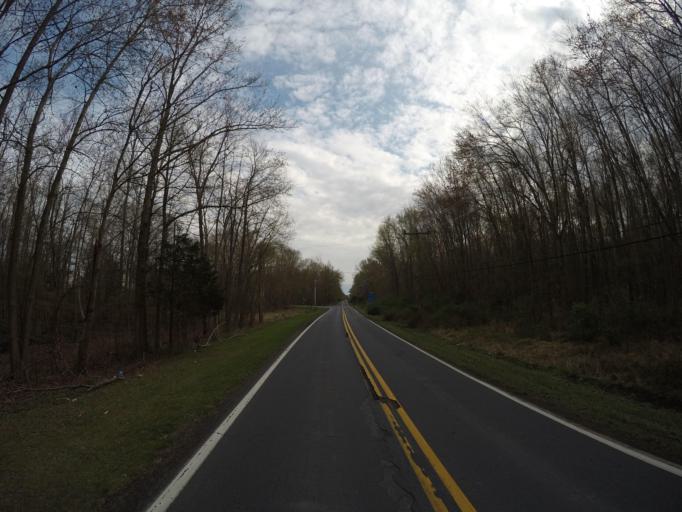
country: US
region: Delaware
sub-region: New Castle County
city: Glasgow
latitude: 39.5750
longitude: -75.7643
